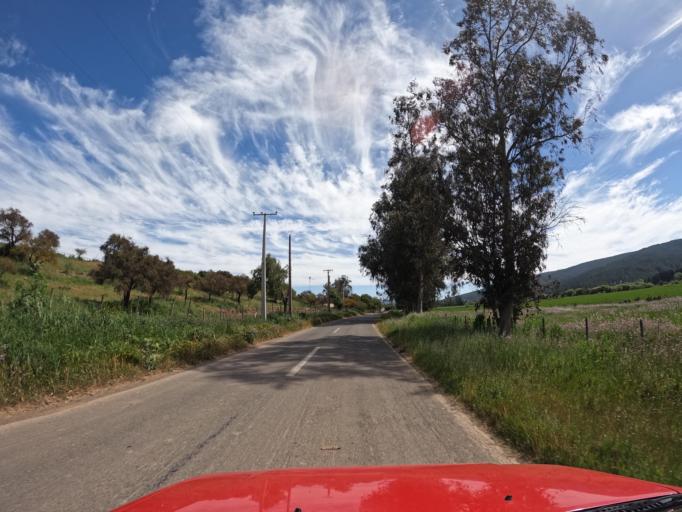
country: CL
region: Maule
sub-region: Provincia de Talca
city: Constitucion
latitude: -35.0053
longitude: -72.0293
